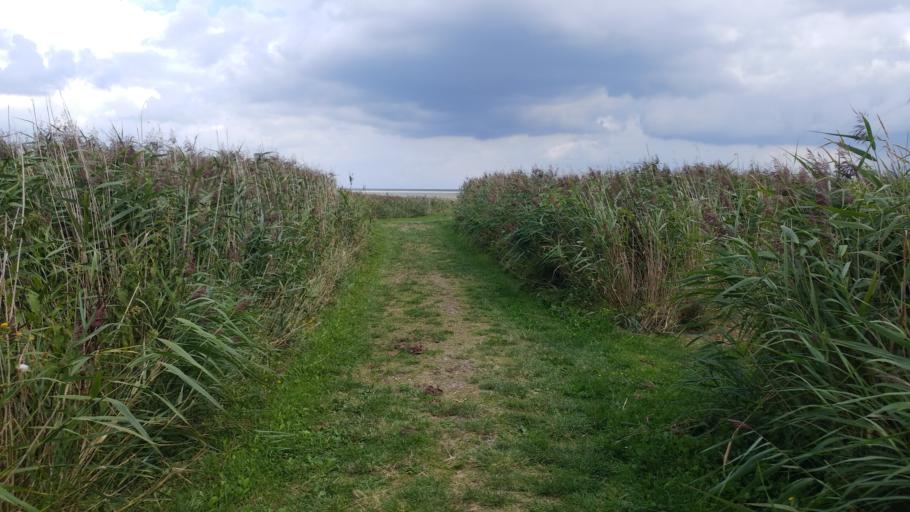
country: DK
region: Central Jutland
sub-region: Norddjurs Kommune
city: Allingabro
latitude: 56.5498
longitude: 10.3747
